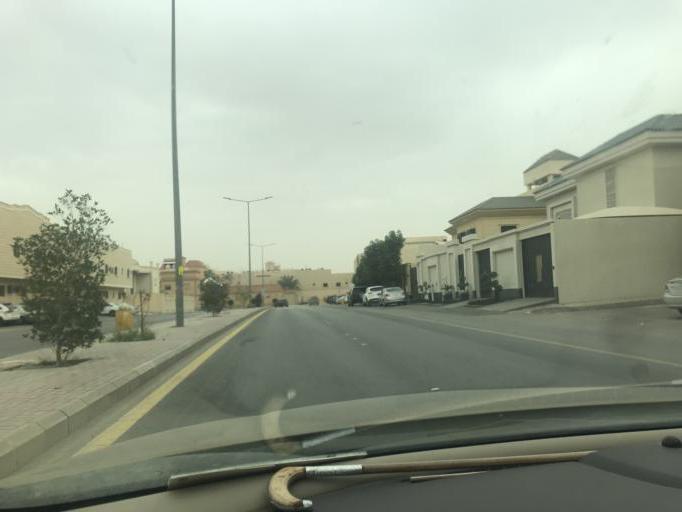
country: SA
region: Ar Riyad
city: Riyadh
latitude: 24.7365
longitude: 46.7570
